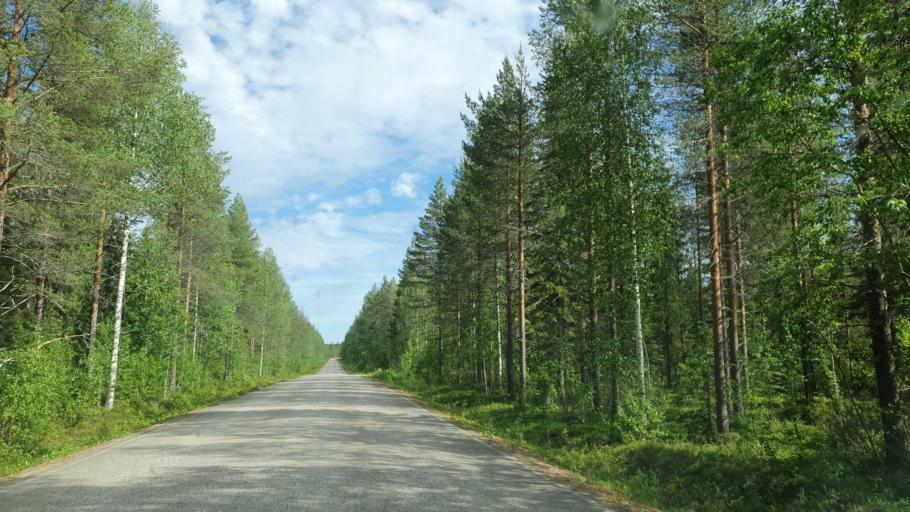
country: FI
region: Kainuu
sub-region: Kehys-Kainuu
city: Kuhmo
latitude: 64.5364
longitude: 29.3224
